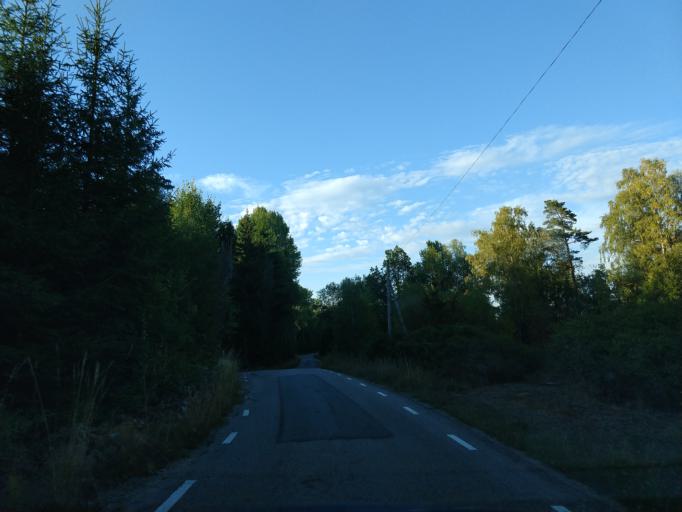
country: SE
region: Blekinge
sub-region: Ronneby Kommun
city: Brakne-Hoby
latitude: 56.2730
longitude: 15.1607
